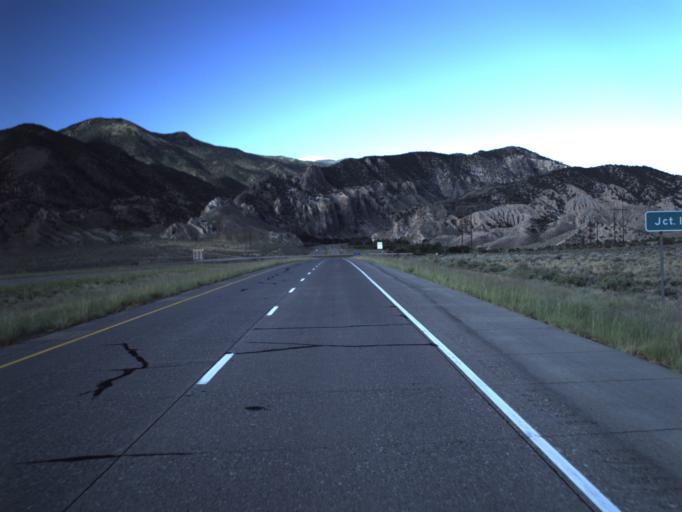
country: US
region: Utah
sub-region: Sevier County
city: Monroe
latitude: 38.5949
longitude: -112.2651
